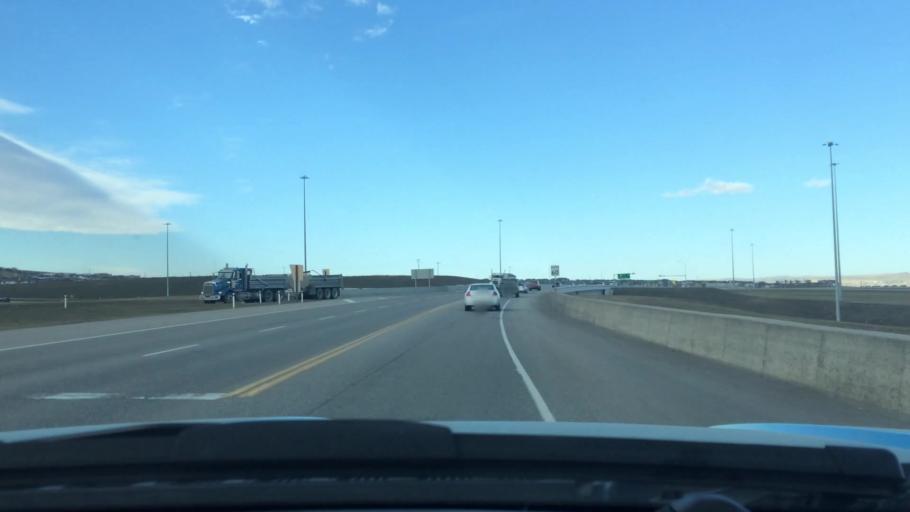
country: CA
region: Alberta
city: Calgary
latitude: 51.1508
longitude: -114.1395
